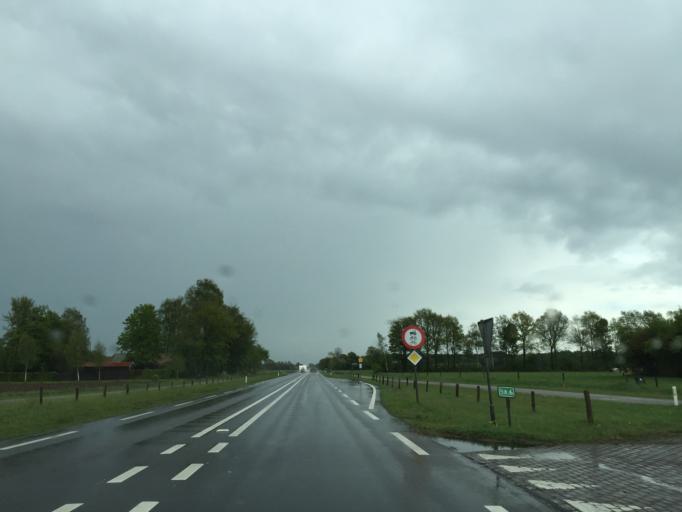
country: NL
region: Overijssel
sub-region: Gemeente Dalfsen
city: Dalfsen
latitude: 52.5292
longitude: 6.2762
